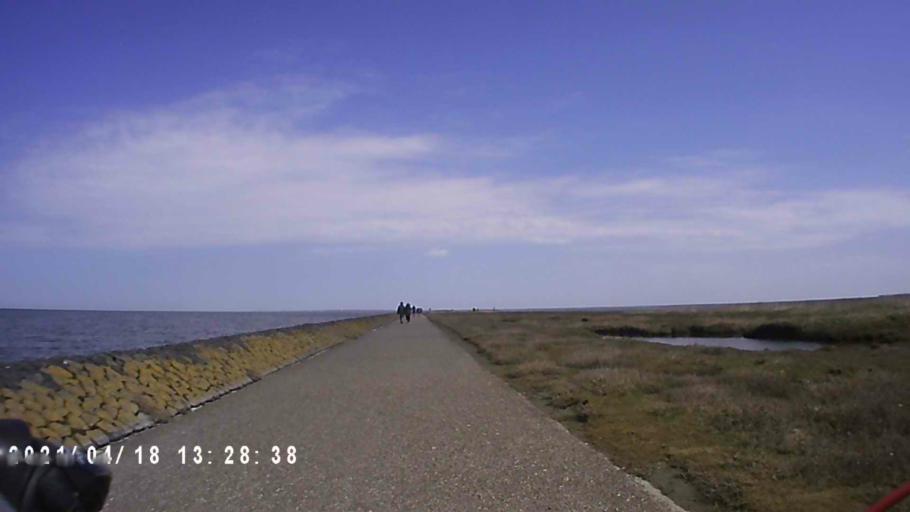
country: NL
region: Friesland
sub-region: Gemeente Dongeradeel
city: Anjum
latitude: 53.4080
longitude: 6.0905
